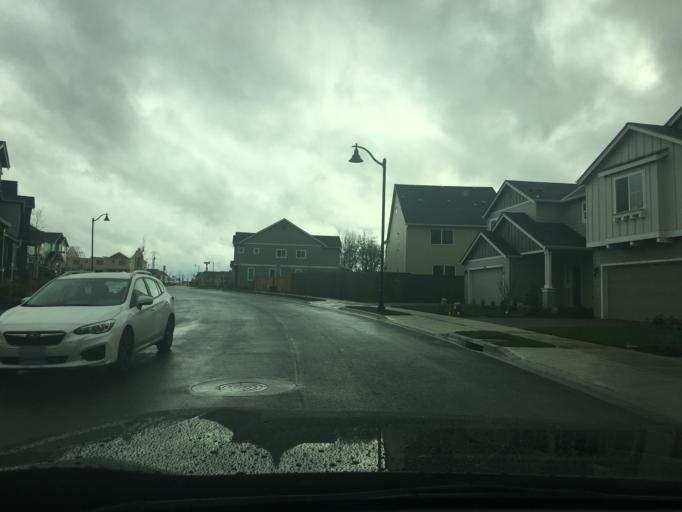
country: US
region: Oregon
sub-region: Washington County
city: Bethany
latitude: 45.5733
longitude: -122.8466
